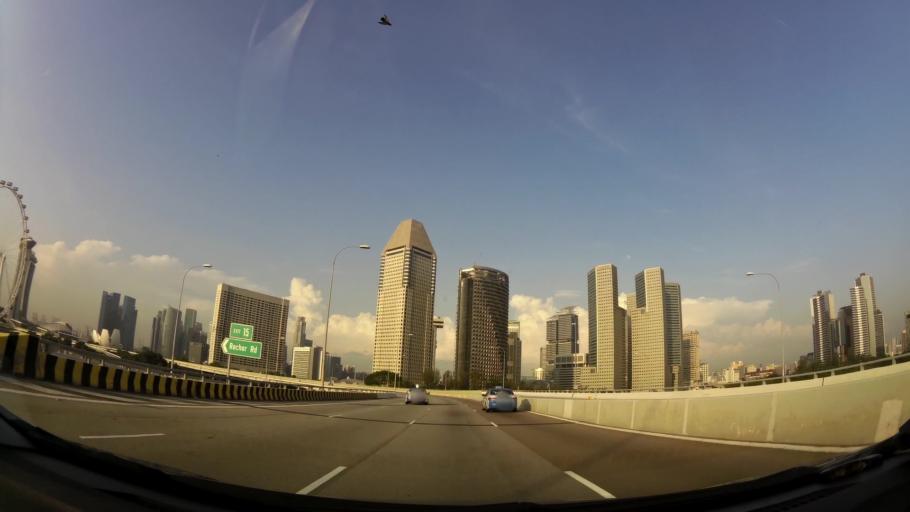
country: SG
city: Singapore
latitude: 1.2939
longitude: 103.8643
